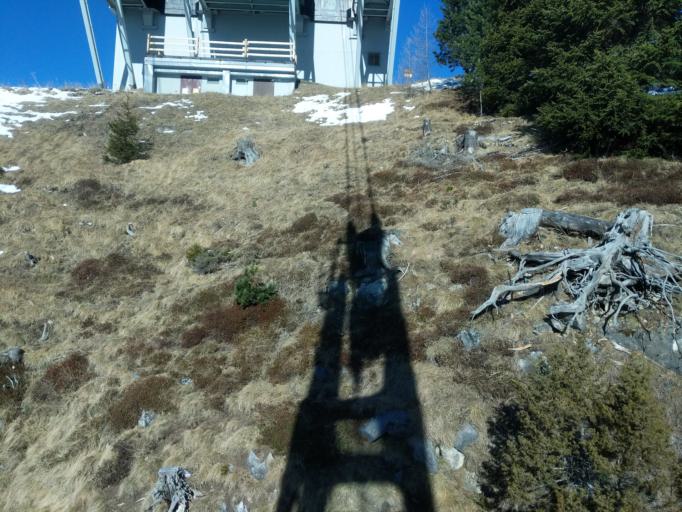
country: IT
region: Trentino-Alto Adige
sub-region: Provincia di Trento
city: Vigo di Fassa
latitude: 46.4331
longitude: 11.6655
